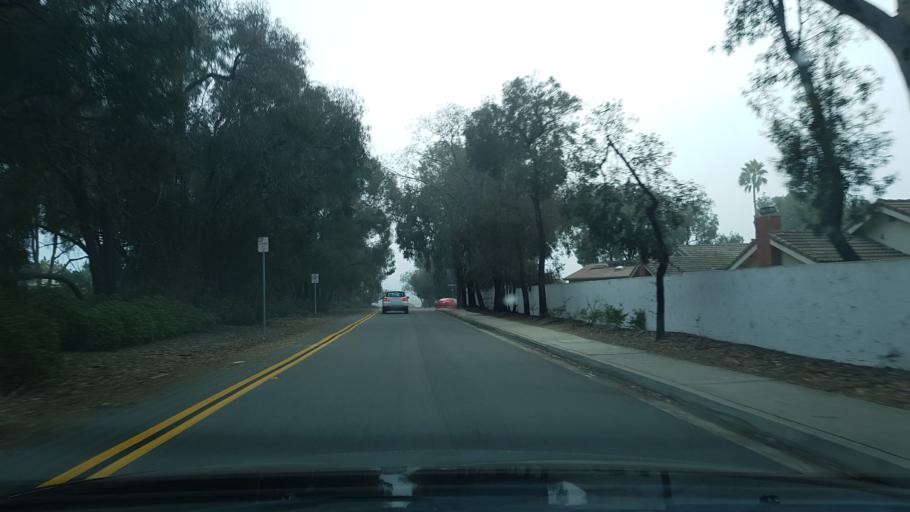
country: US
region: California
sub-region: San Diego County
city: La Jolla
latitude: 32.8580
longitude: -117.2402
